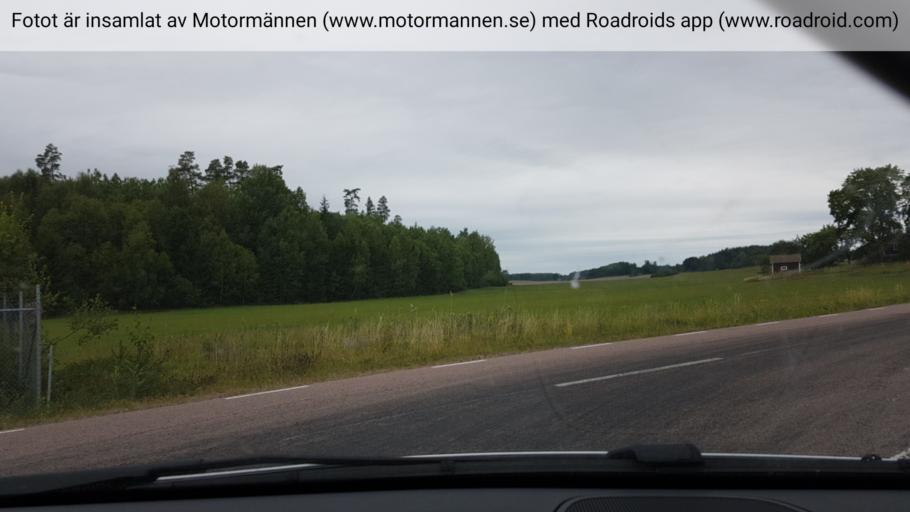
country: SE
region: Soedermanland
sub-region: Strangnas Kommun
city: Stallarholmen
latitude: 59.3395
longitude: 17.2269
